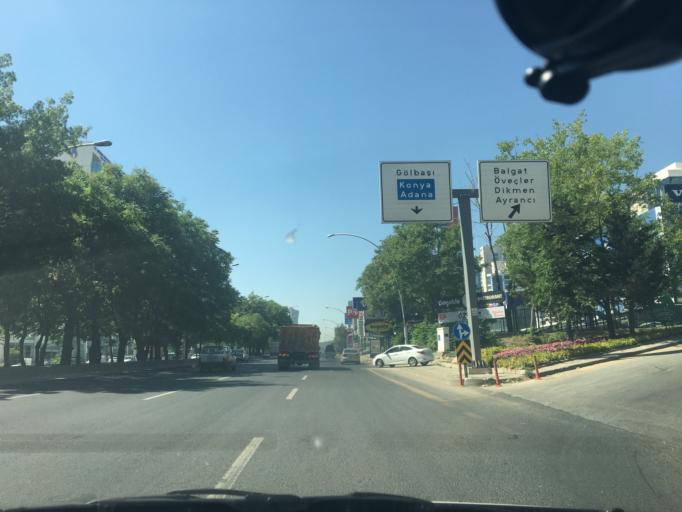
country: TR
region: Ankara
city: Ankara
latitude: 39.8969
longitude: 32.8133
